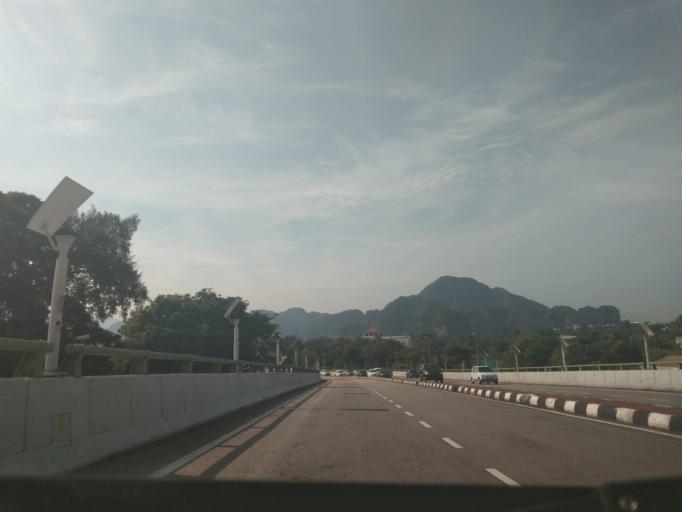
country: MY
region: Perak
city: Ipoh
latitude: 4.5780
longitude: 101.1065
